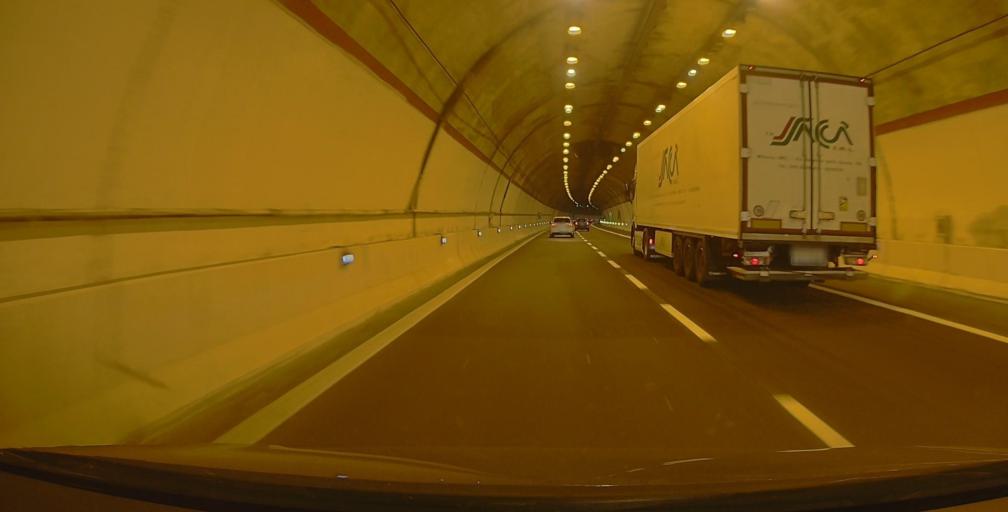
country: IT
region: Calabria
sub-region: Provincia di Vibo-Valentia
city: Francica
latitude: 38.5772
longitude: 16.1208
